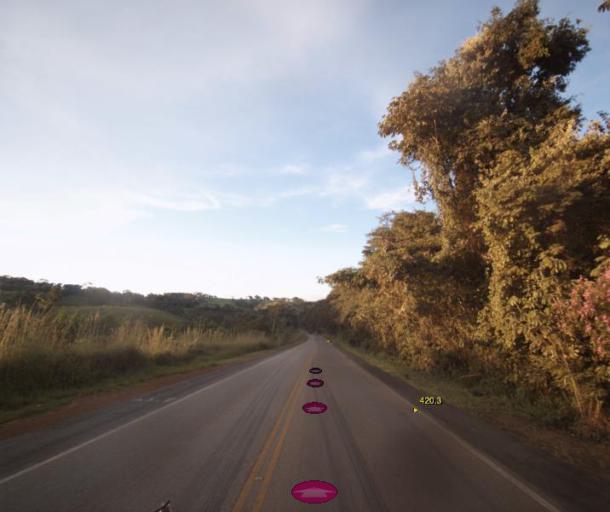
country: BR
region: Goias
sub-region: Abadiania
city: Abadiania
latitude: -16.1268
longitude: -48.8950
